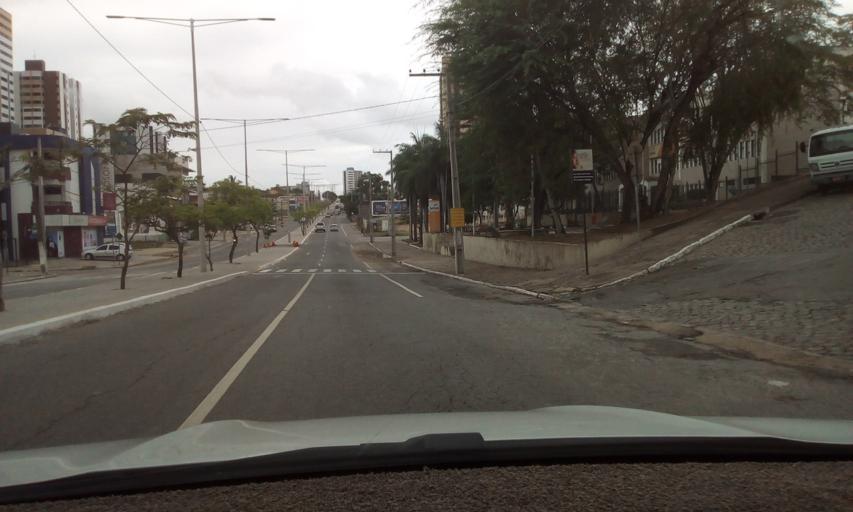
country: BR
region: Paraiba
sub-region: Campina Grande
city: Campina Grande
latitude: -7.2141
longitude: -35.8772
